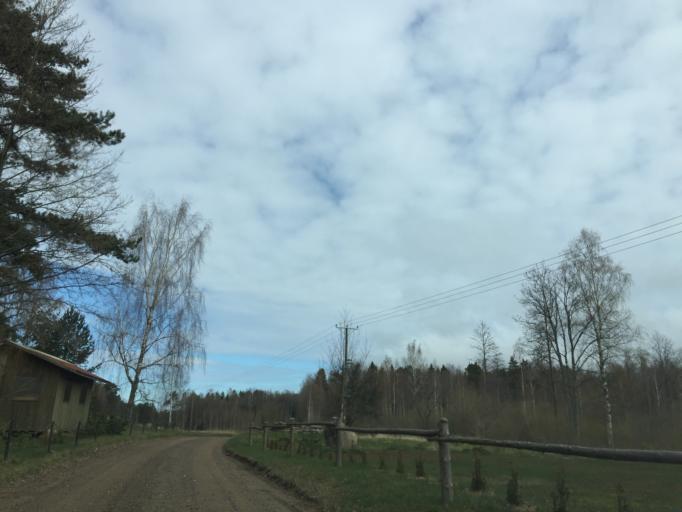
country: LV
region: Salacgrivas
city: Salacgriva
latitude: 57.5267
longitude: 24.3788
